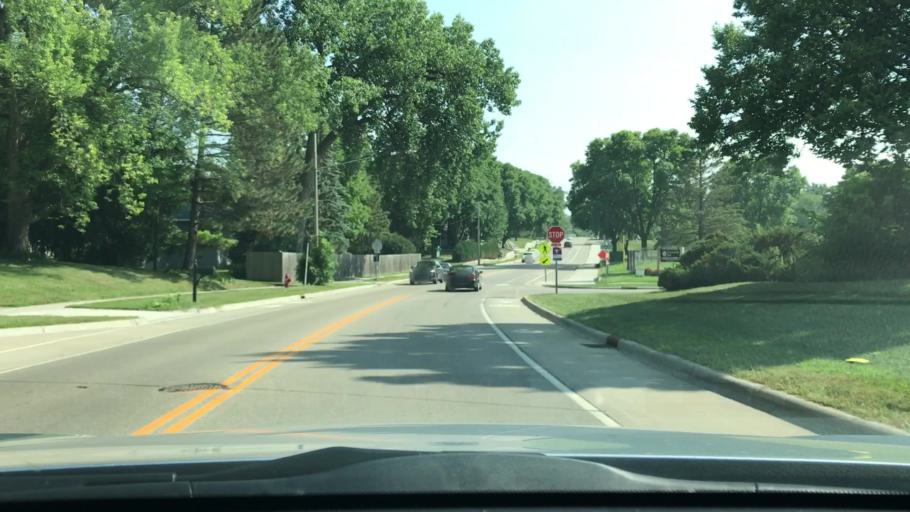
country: US
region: Minnesota
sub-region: Hennepin County
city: Edina
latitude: 44.8920
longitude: -93.3690
